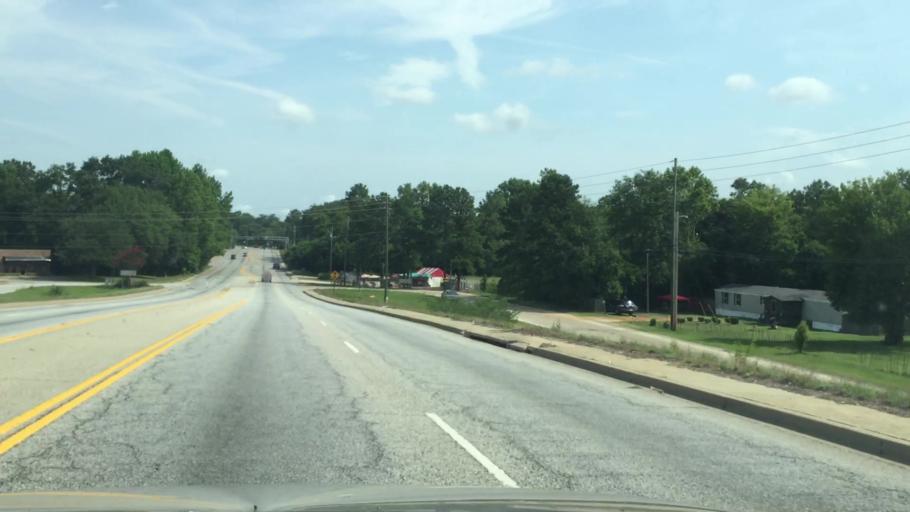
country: US
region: South Carolina
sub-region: Sumter County
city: South Sumter
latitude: 33.9071
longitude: -80.3539
